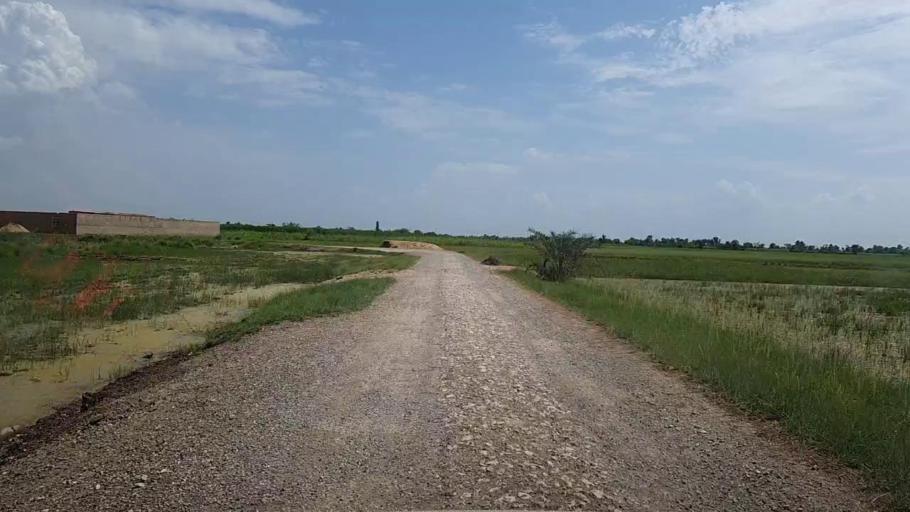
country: PK
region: Sindh
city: Bhiria
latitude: 26.9459
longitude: 68.2432
